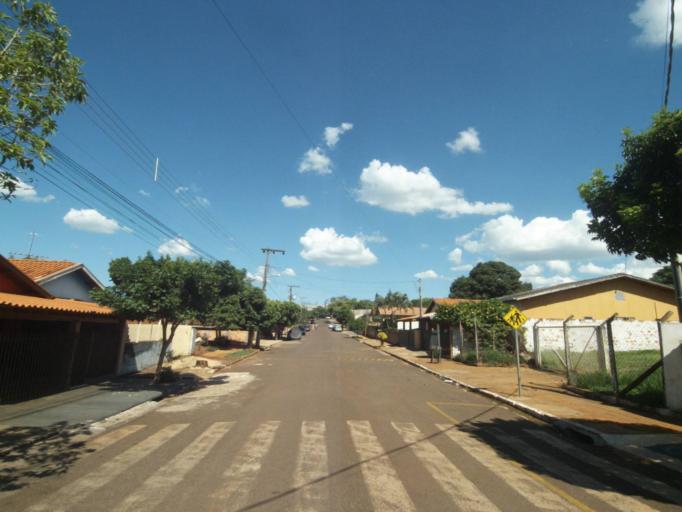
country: BR
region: Parana
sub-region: Sertanopolis
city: Sertanopolis
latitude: -23.0426
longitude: -50.8213
